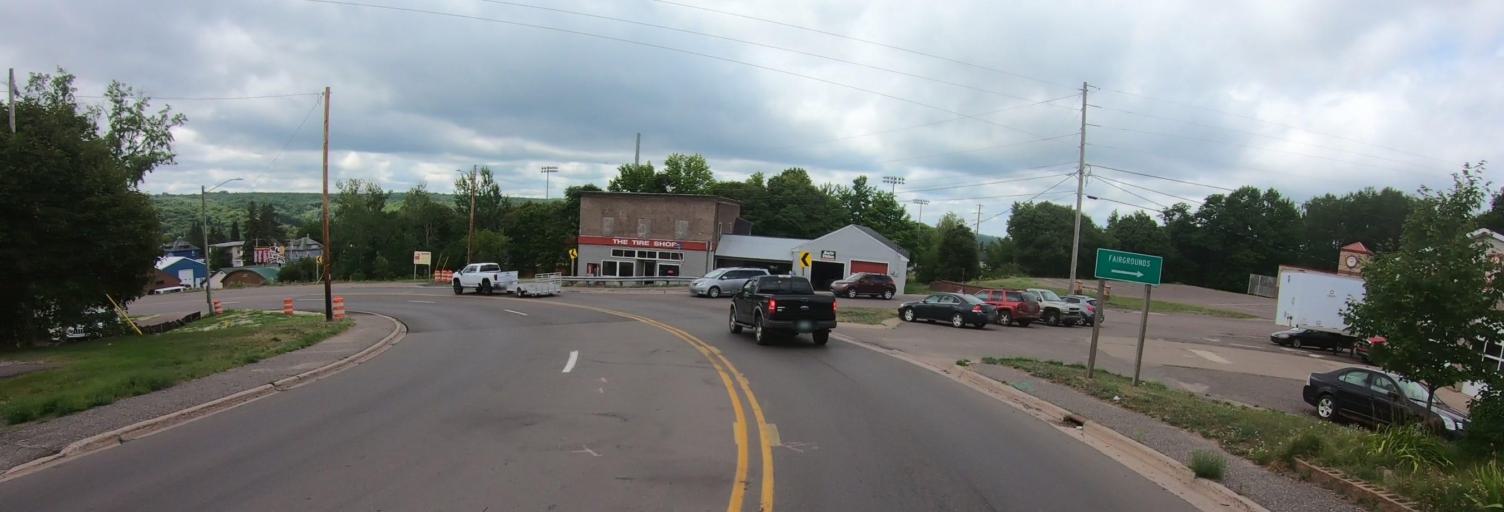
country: US
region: Michigan
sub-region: Houghton County
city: Hancock
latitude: 47.1305
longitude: -88.5990
